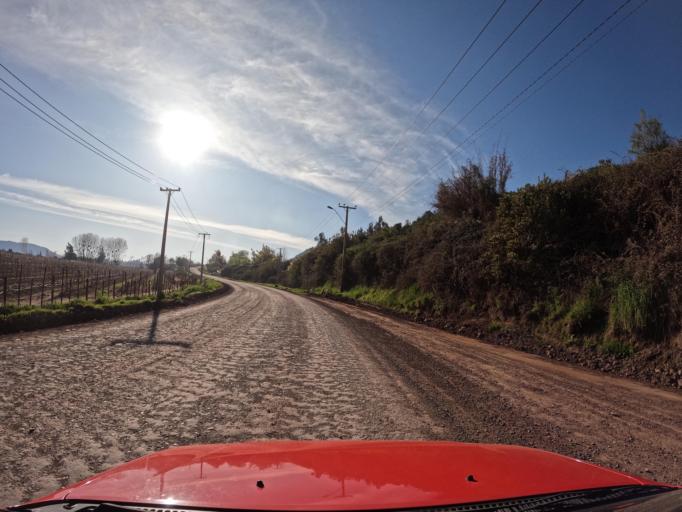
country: CL
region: Maule
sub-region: Provincia de Curico
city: Teno
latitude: -34.9670
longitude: -70.9485
